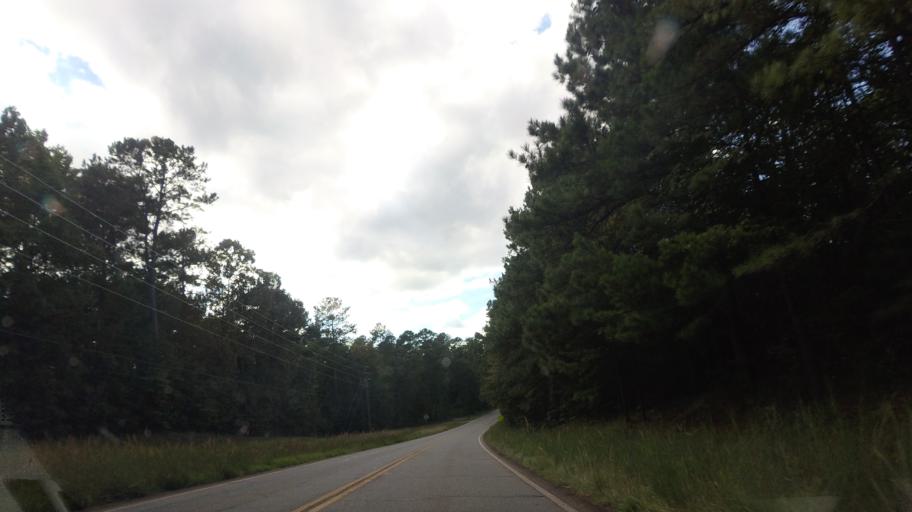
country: US
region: Georgia
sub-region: Monroe County
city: Forsyth
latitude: 33.0280
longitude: -83.8082
